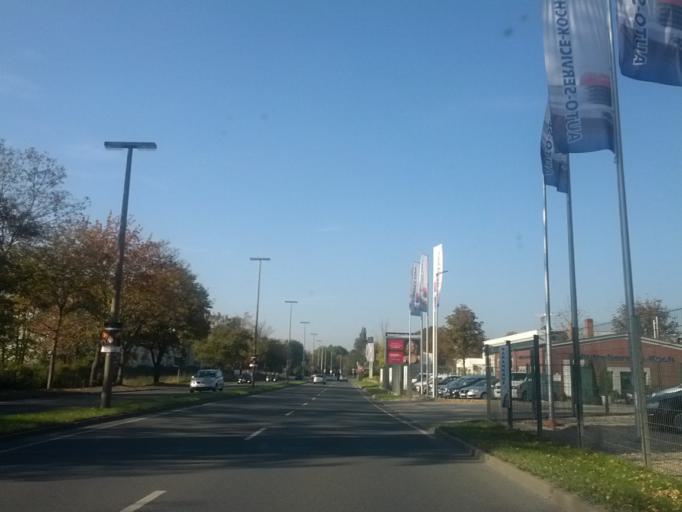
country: DE
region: Thuringia
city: Gera
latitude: 50.9005
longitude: 12.0714
